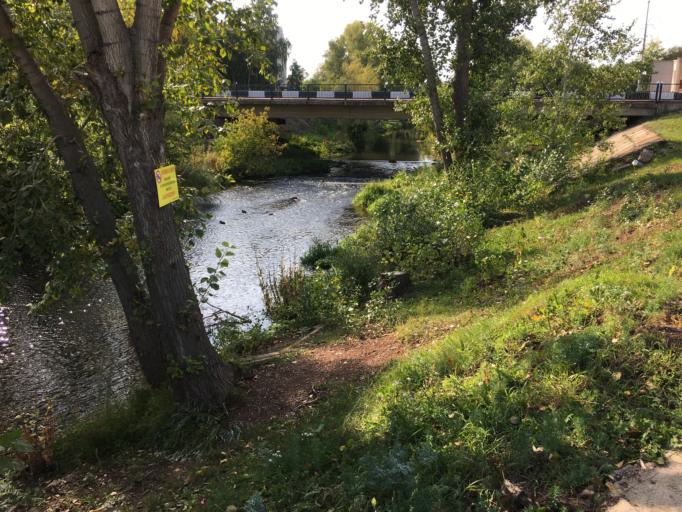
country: RU
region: Bashkortostan
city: Meleuz
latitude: 52.9599
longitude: 55.9345
